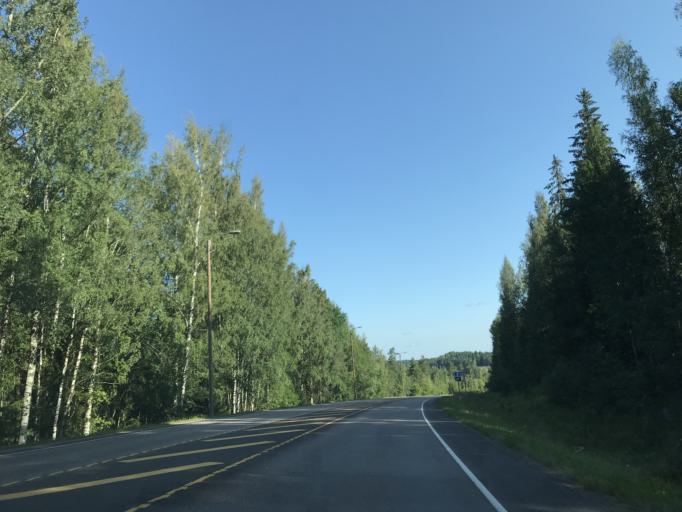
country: FI
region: Paijanne Tavastia
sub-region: Lahti
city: Lahti
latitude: 61.0443
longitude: 25.6645
